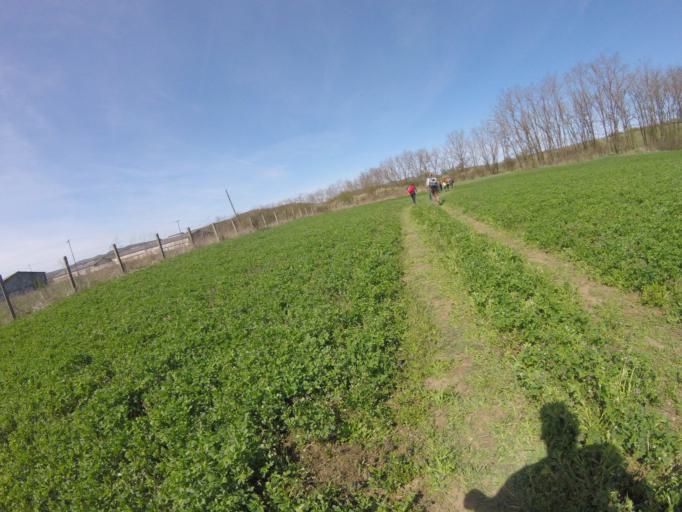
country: HU
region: Borsod-Abauj-Zemplen
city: Szendro
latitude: 48.4167
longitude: 20.7672
